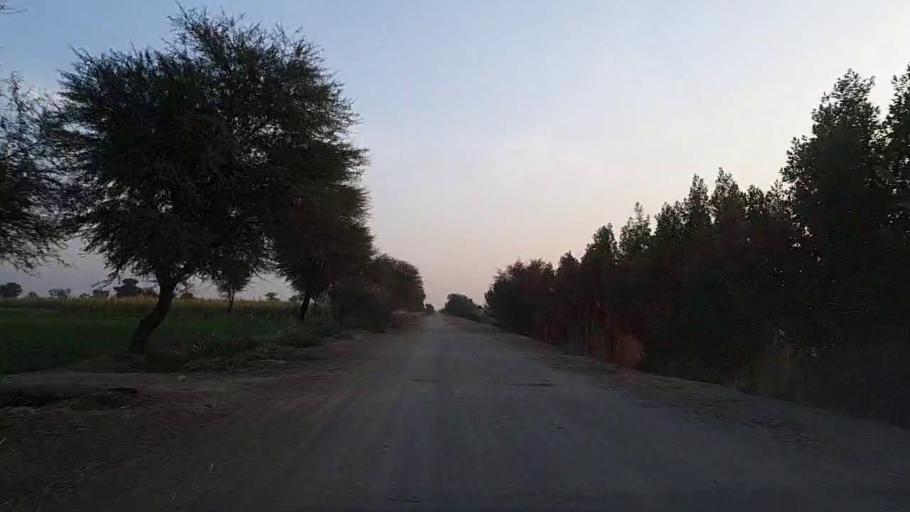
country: PK
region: Sindh
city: Tando Mittha Khan
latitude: 25.9754
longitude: 69.1105
